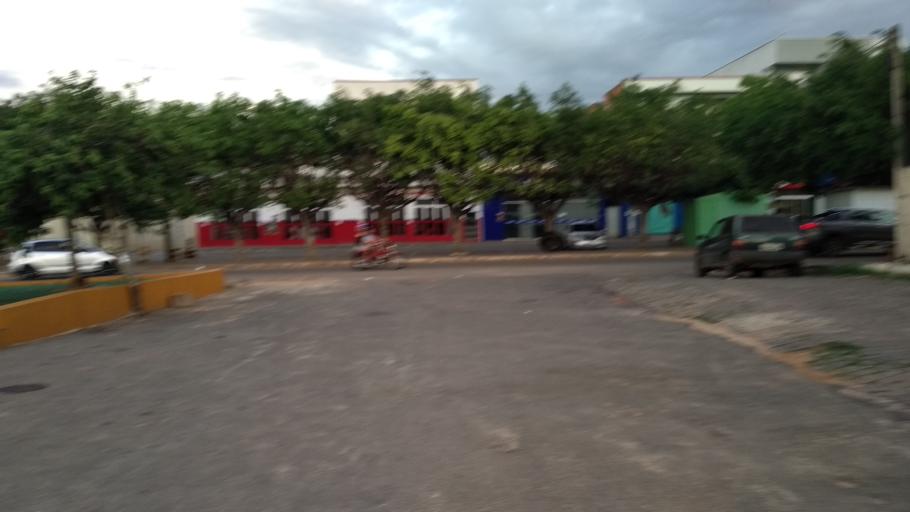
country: BR
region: Bahia
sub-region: Caetite
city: Caetite
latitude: -14.0653
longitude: -42.4902
